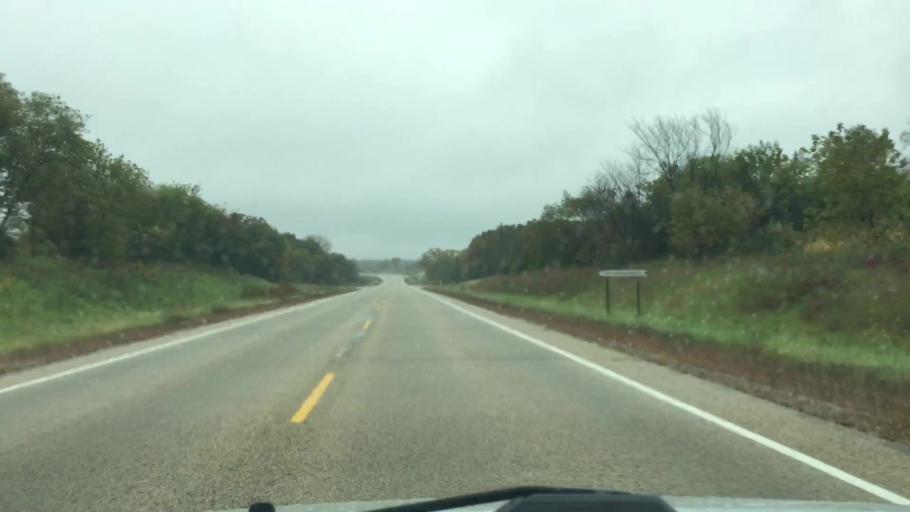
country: US
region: Wisconsin
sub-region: Jefferson County
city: Palmyra
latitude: 42.8820
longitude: -88.5549
